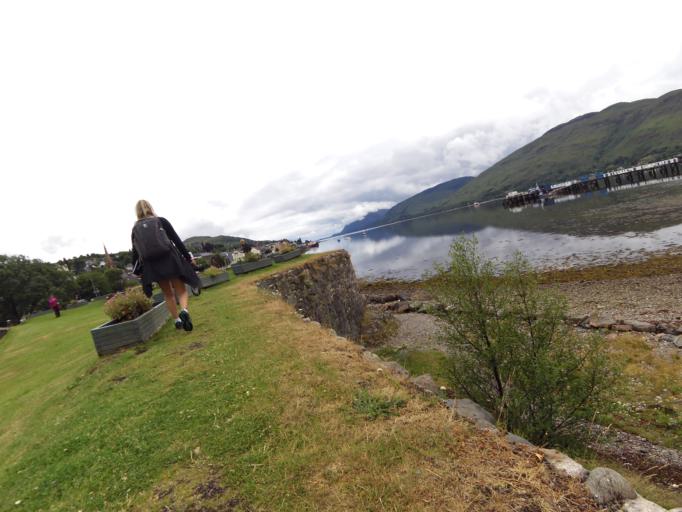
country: GB
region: Scotland
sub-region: Highland
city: Fort William
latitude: 56.8215
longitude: -5.1081
